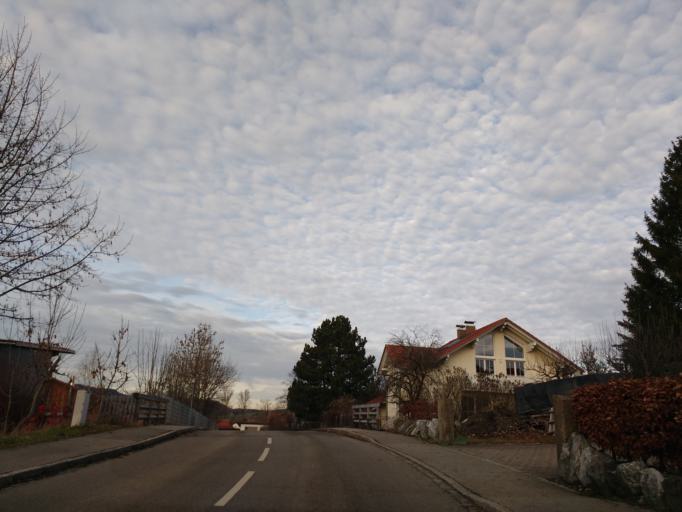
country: DE
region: Bavaria
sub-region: Swabia
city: Wildpoldsried
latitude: 47.7691
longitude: 10.3993
